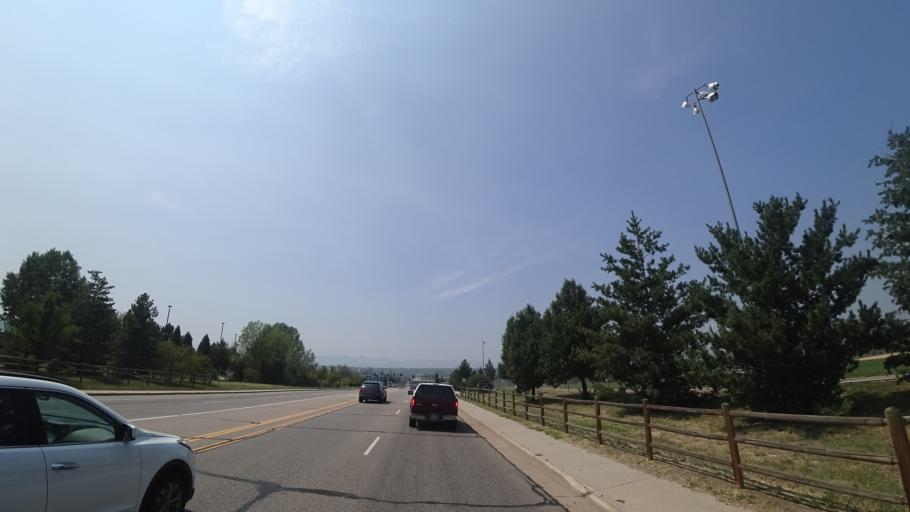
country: US
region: Colorado
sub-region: Arapahoe County
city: Littleton
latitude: 39.6241
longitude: -105.0043
